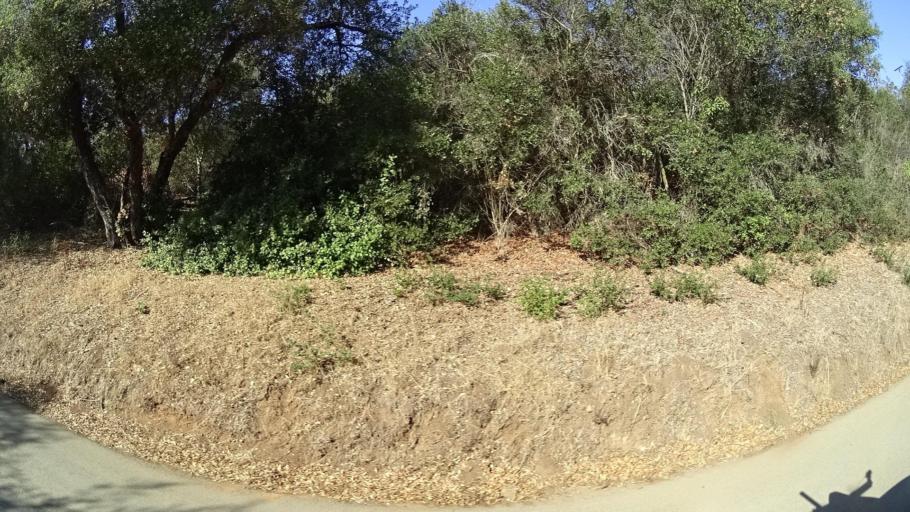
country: US
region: California
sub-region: San Diego County
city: Lake San Marcos
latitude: 33.0948
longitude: -117.1716
